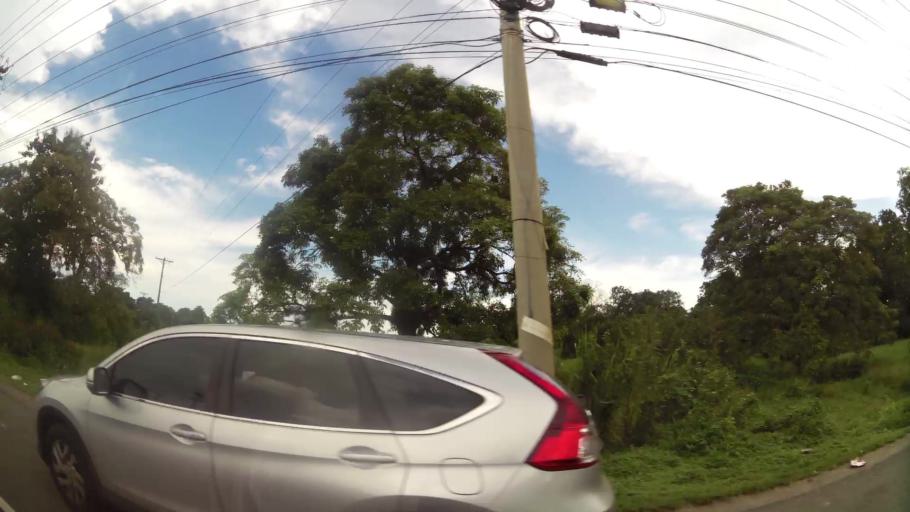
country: PA
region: Panama
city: Tocumen
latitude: 9.0693
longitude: -79.3937
